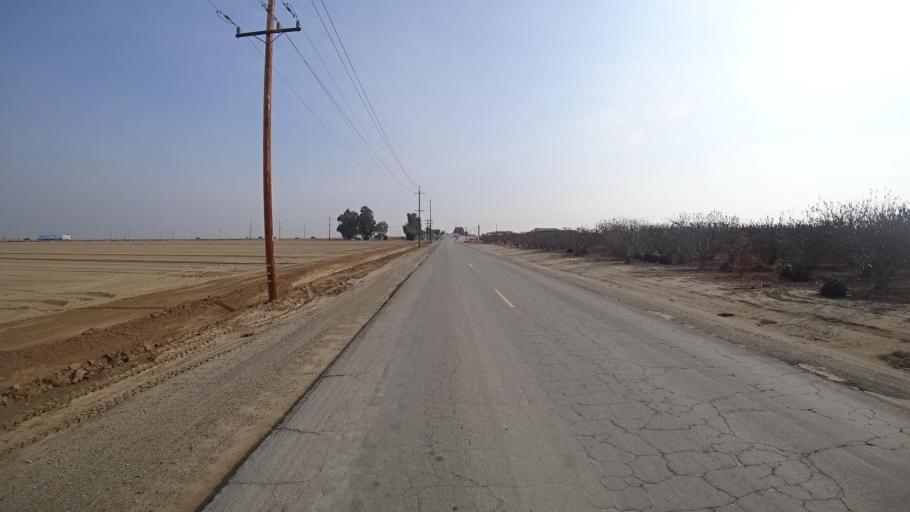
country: US
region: California
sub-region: Kern County
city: Greenfield
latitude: 35.0951
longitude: -119.0433
